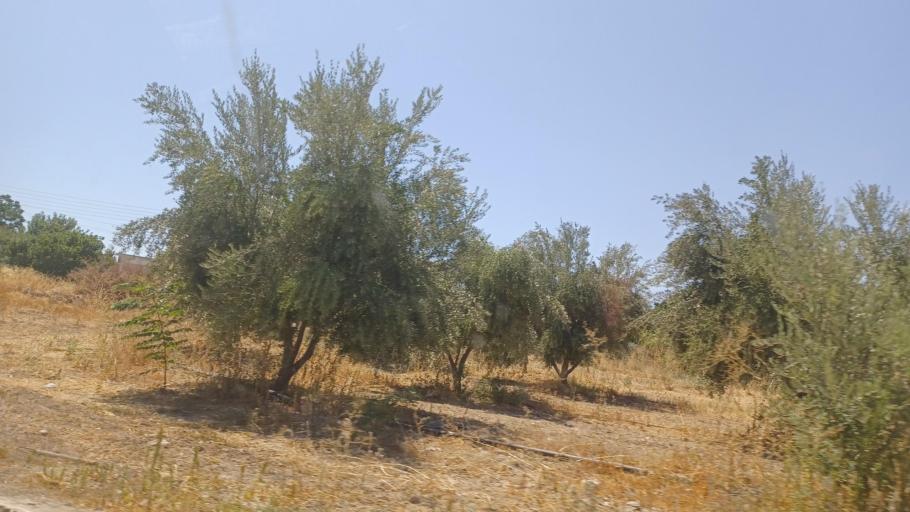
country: CY
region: Pafos
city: Polis
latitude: 35.0523
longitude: 32.4758
